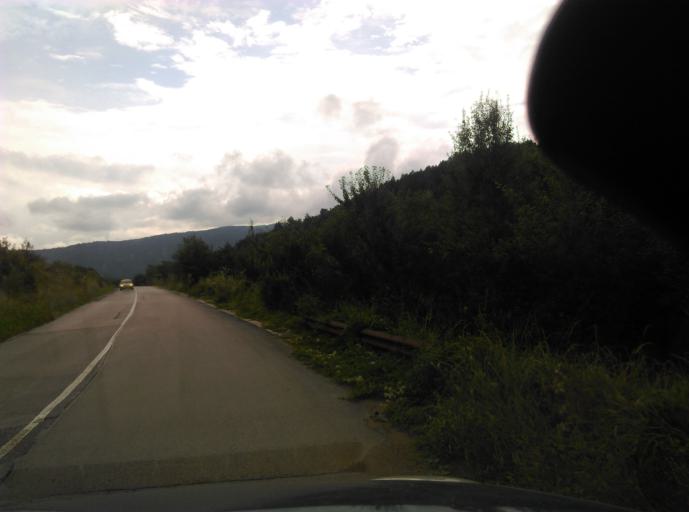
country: BG
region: Sofia-Capital
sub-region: Stolichna Obshtina
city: Sofia
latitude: 42.5852
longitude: 23.3883
